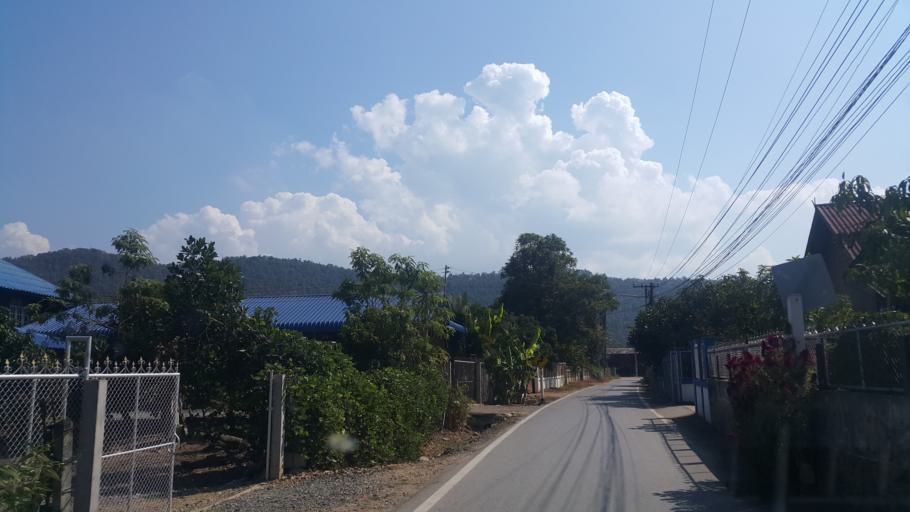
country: TH
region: Chiang Mai
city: San Kamphaeng
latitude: 18.6975
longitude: 99.1643
